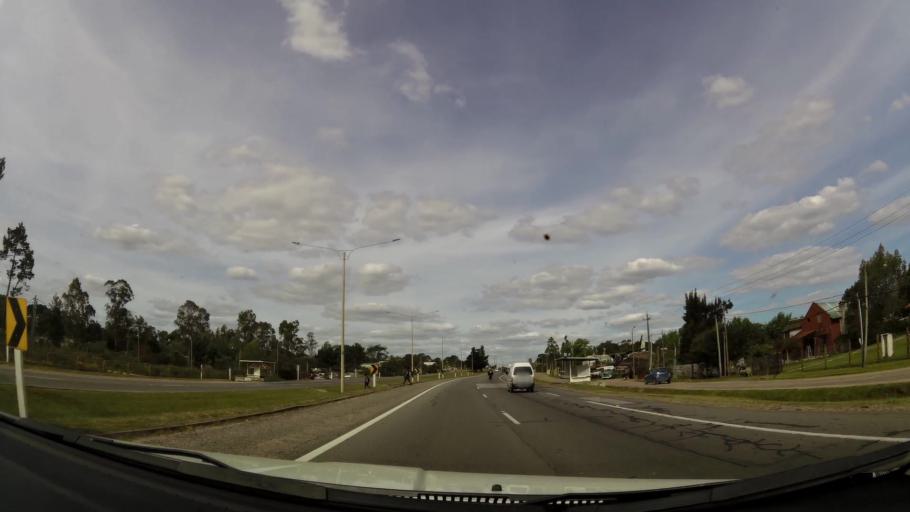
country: UY
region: Canelones
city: Empalme Olmos
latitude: -34.7793
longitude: -55.8682
